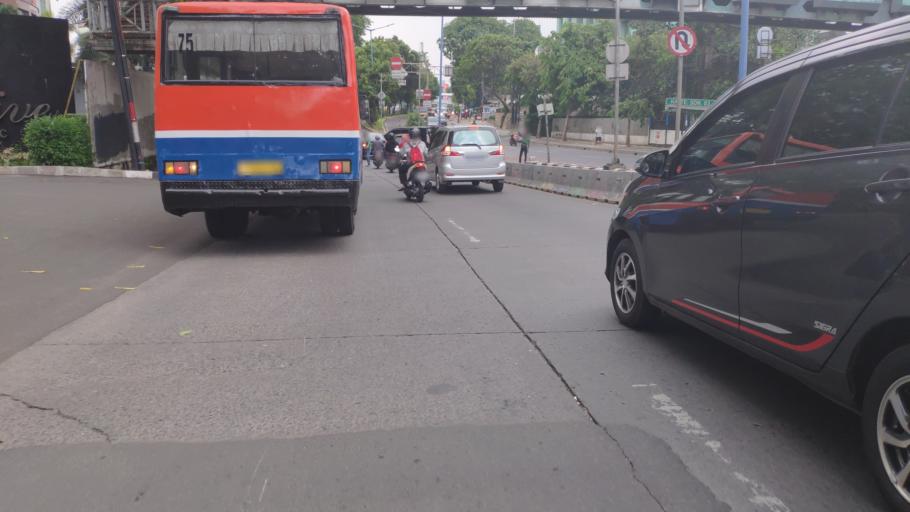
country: ID
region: Jakarta Raya
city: Jakarta
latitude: -6.2767
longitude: 106.8302
